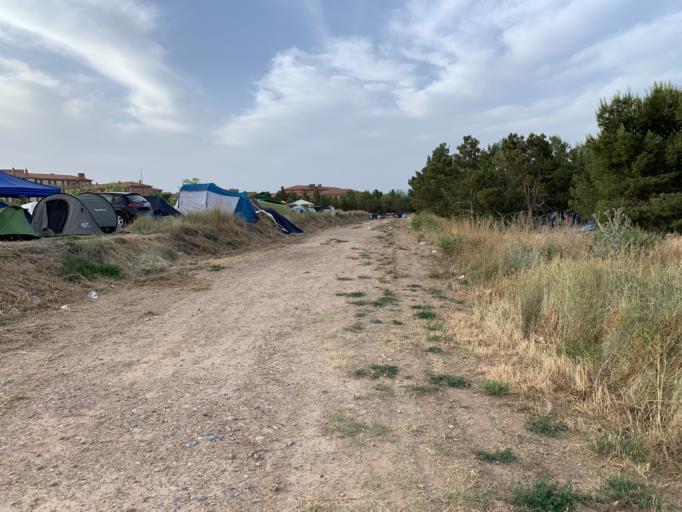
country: ES
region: Aragon
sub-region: Provincia de Teruel
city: Teruel
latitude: 40.3506
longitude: -1.1150
